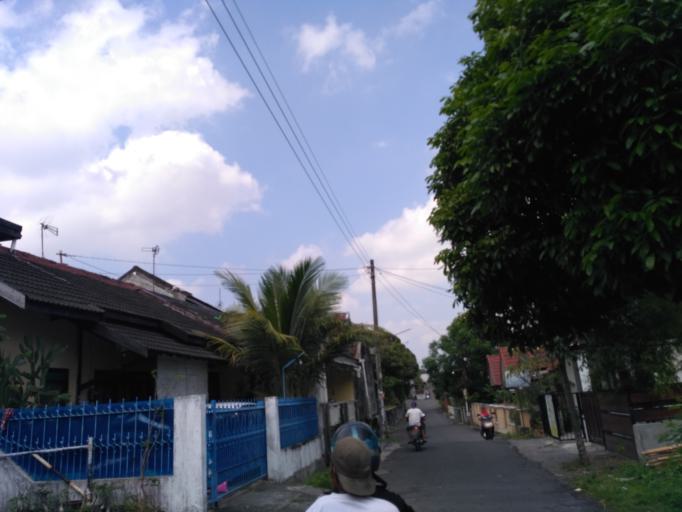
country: ID
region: Daerah Istimewa Yogyakarta
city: Depok
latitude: -7.7413
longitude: 110.4100
